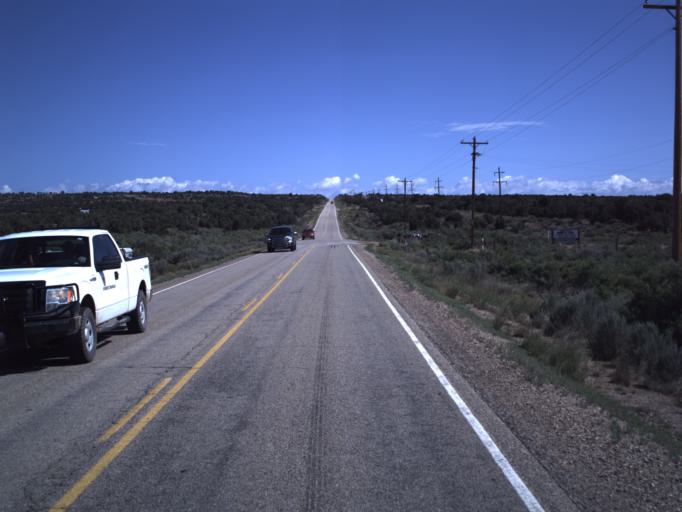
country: US
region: Utah
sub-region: Duchesne County
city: Duchesne
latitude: 40.2850
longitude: -110.3772
